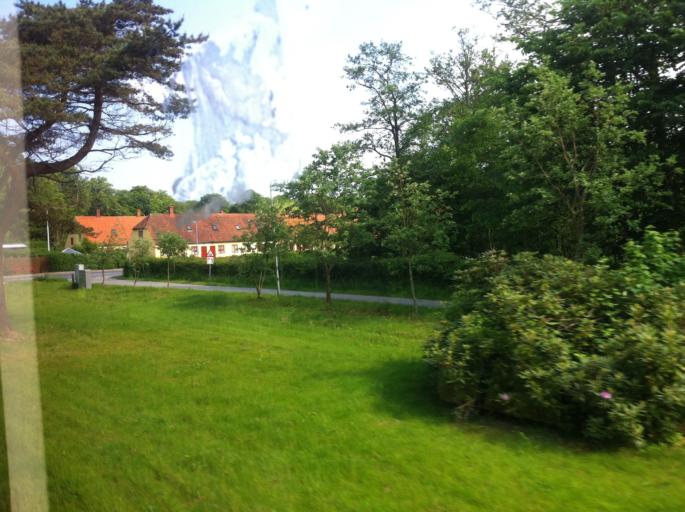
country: DK
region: Capital Region
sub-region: Helsingor Kommune
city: Hellebaek
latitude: 56.0667
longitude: 12.5539
